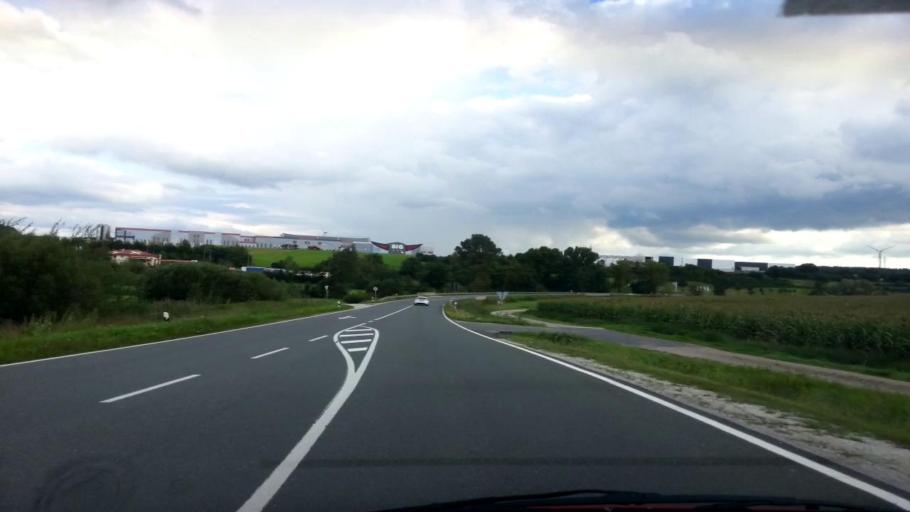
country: DE
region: Bavaria
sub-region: Upper Franconia
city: Schlusselfeld
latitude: 49.7419
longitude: 10.6334
